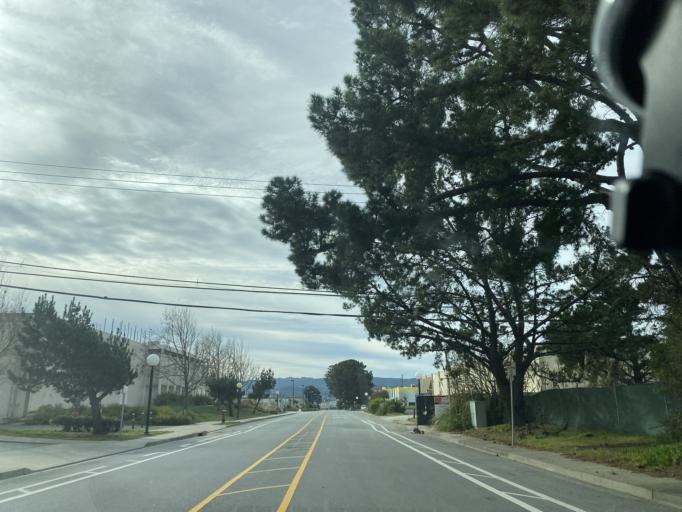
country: US
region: California
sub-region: San Mateo County
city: South San Francisco
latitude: 37.6551
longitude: -122.3897
